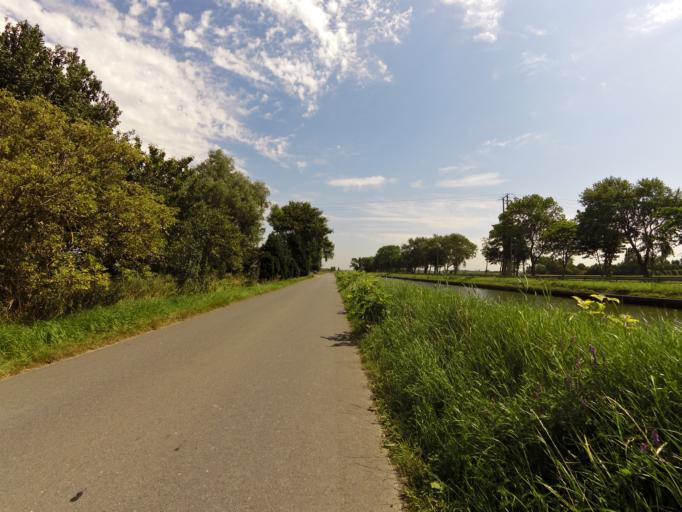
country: BE
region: Flanders
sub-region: Provincie West-Vlaanderen
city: Gistel
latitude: 51.1818
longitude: 2.9663
